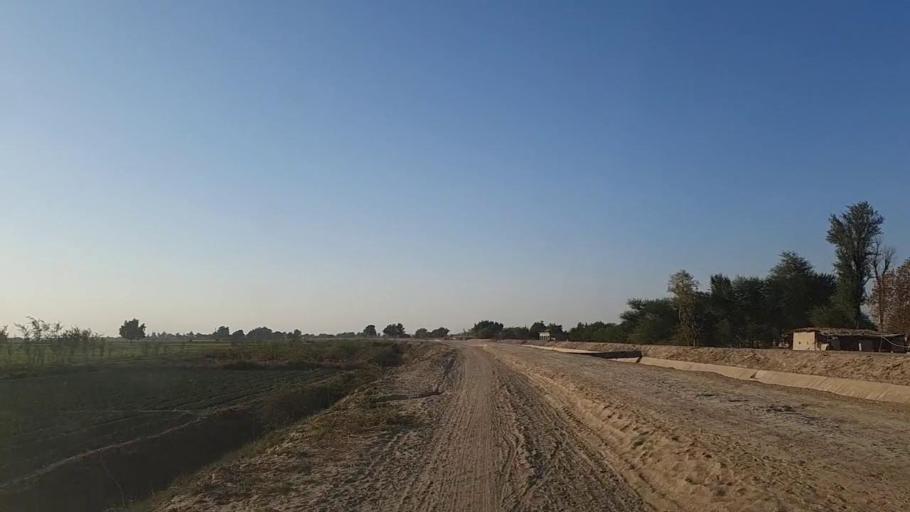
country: PK
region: Sindh
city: Naukot
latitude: 25.0029
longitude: 69.3951
